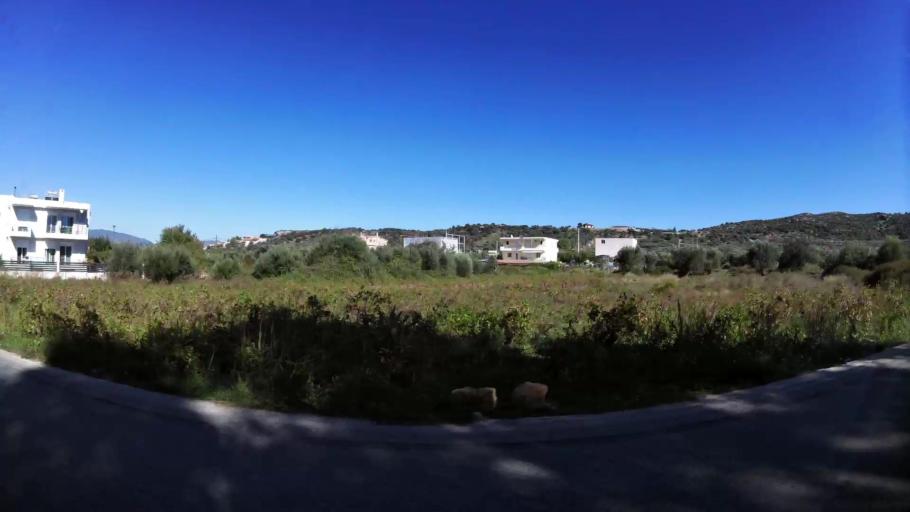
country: GR
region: Attica
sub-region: Nomarchia Anatolikis Attikis
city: Paiania
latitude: 37.9670
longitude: 23.8634
